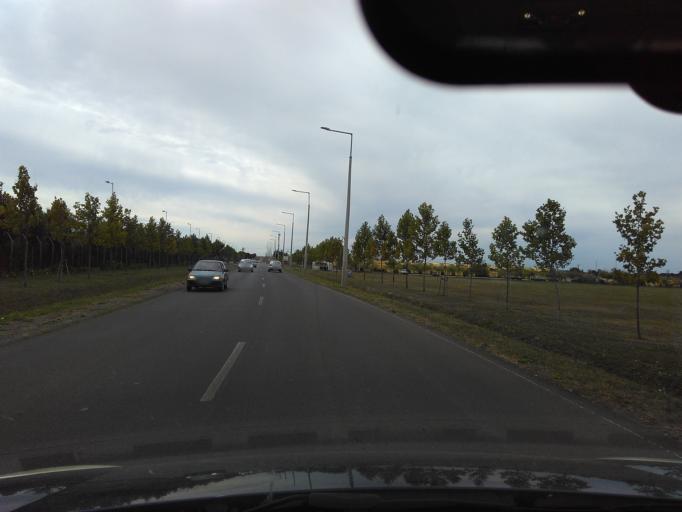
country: HU
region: Heves
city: Hatvan
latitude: 47.6759
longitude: 19.6536
